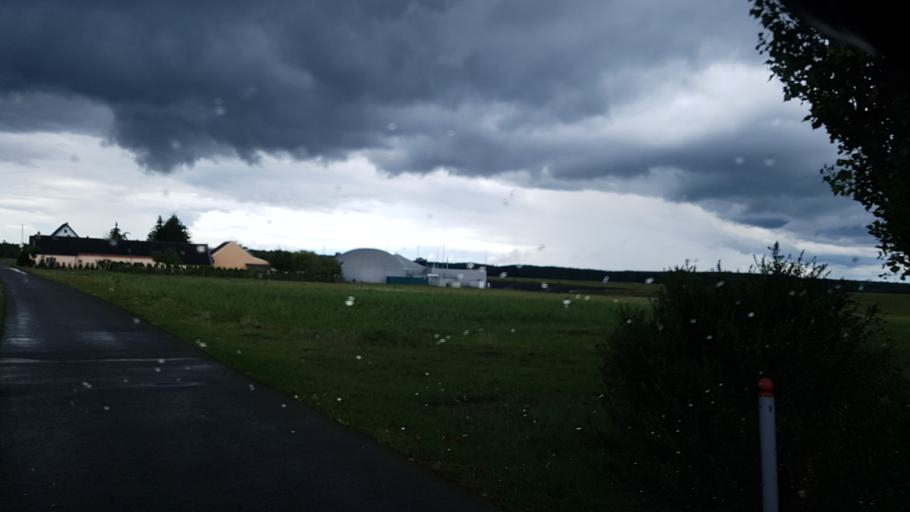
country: DE
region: Saxony
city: Gross Duben
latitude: 51.6316
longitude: 14.5296
